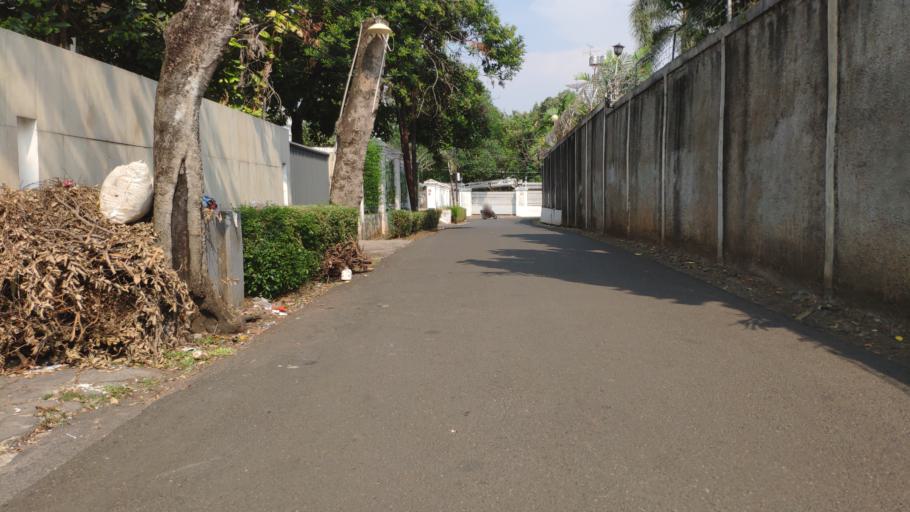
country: ID
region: Jakarta Raya
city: Jakarta
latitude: -6.2735
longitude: 106.8234
